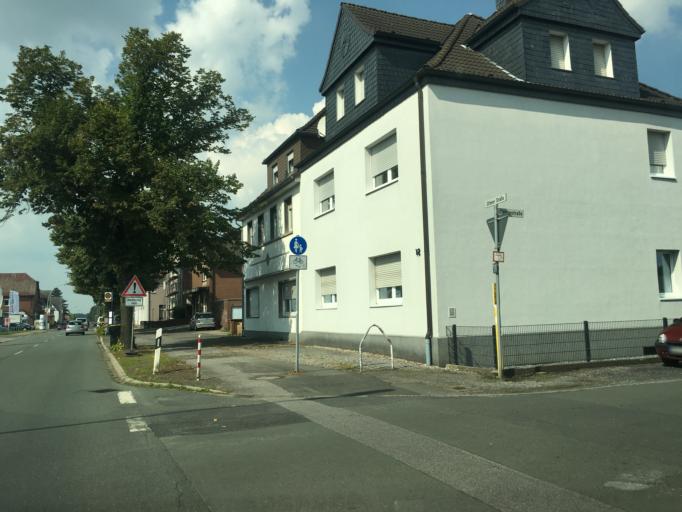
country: DE
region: North Rhine-Westphalia
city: Selm
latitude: 51.7057
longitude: 7.4565
